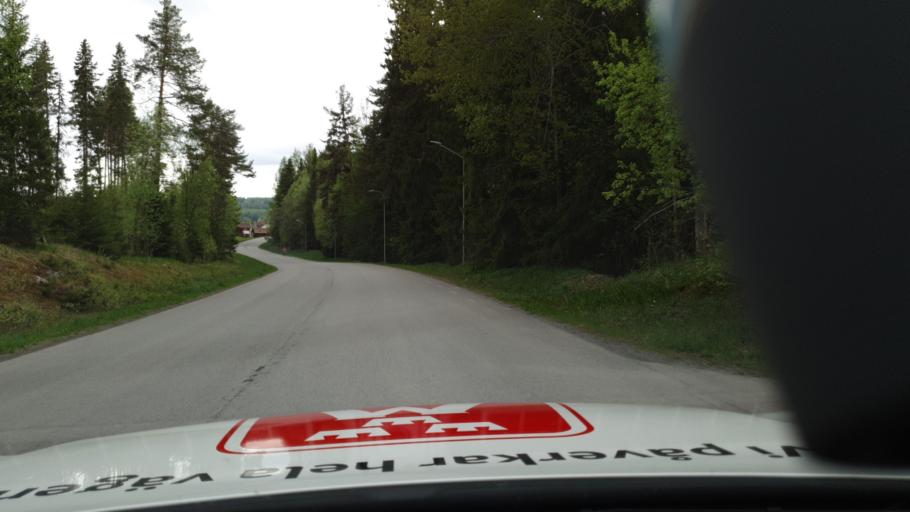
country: SE
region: Jaemtland
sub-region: OEstersunds Kommun
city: Lit
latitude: 63.3233
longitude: 14.8488
